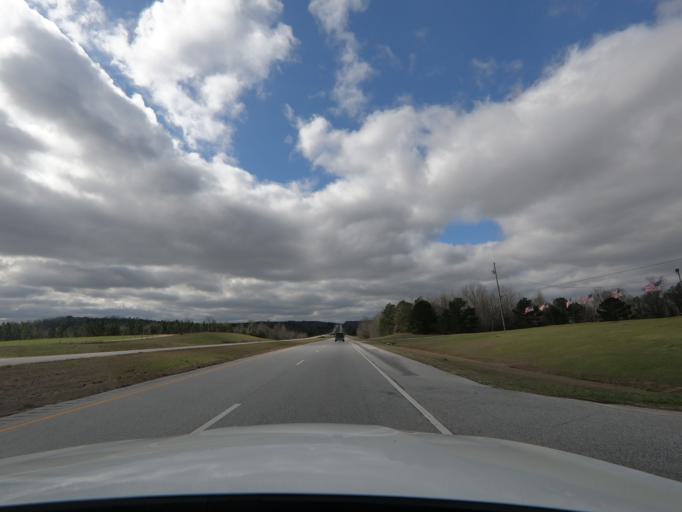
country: US
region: Alabama
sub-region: Russell County
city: Ladonia
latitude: 32.3615
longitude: -85.1043
